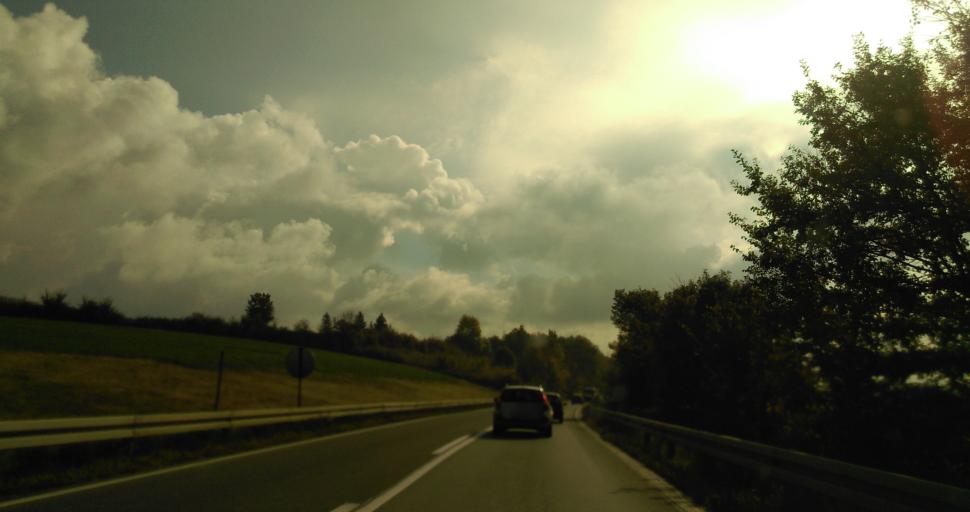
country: RS
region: Central Serbia
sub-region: Belgrade
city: Lazarevac
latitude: 44.3073
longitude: 20.2524
